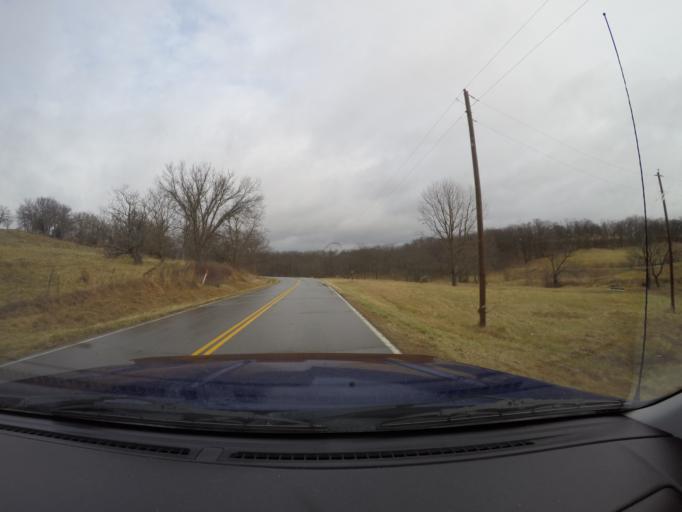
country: US
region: Kansas
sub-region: Jefferson County
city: Oskaloosa
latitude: 39.3365
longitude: -95.1365
